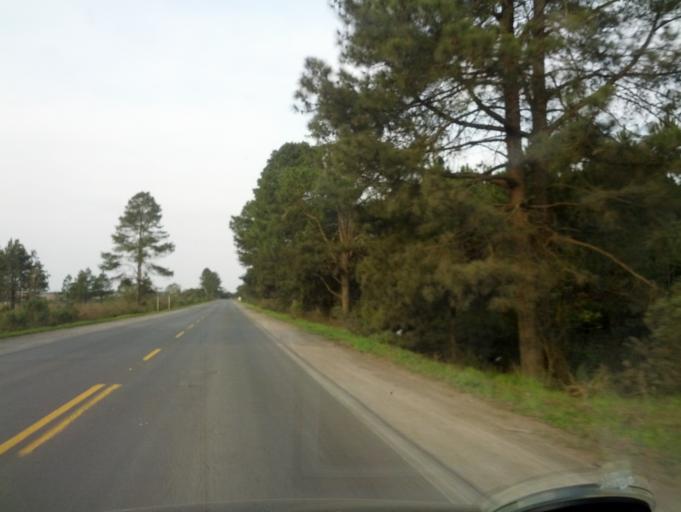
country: BR
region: Santa Catarina
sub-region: Otacilio Costa
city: Otacilio Costa
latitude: -27.3090
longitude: -50.1168
